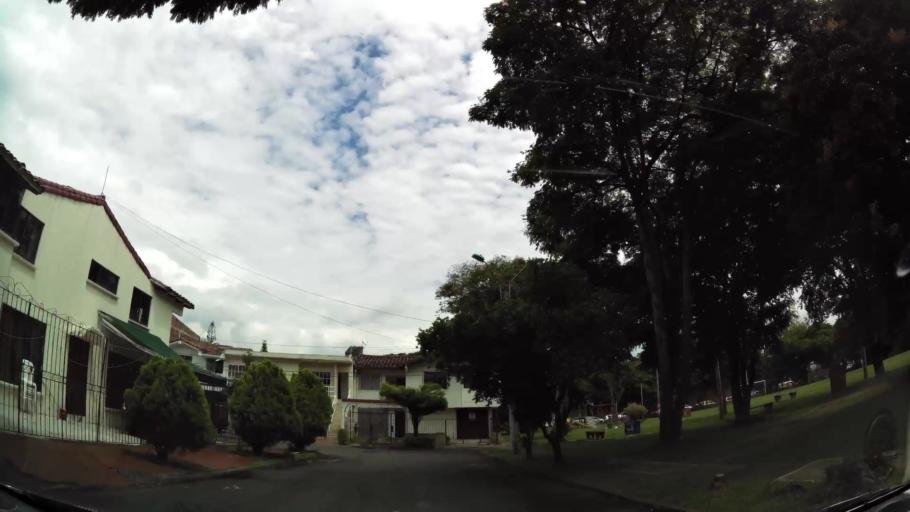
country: CO
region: Valle del Cauca
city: Cali
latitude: 3.3930
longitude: -76.5407
